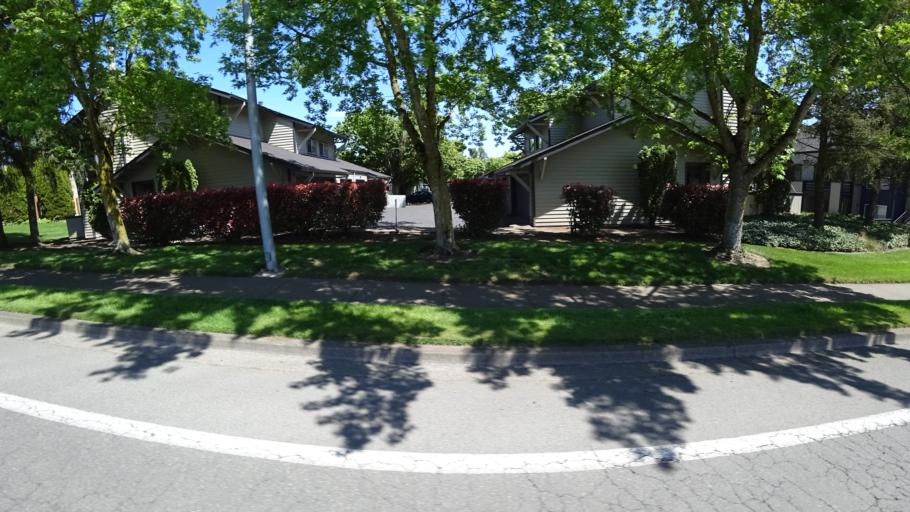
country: US
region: Oregon
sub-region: Washington County
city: King City
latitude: 45.4412
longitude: -122.8259
